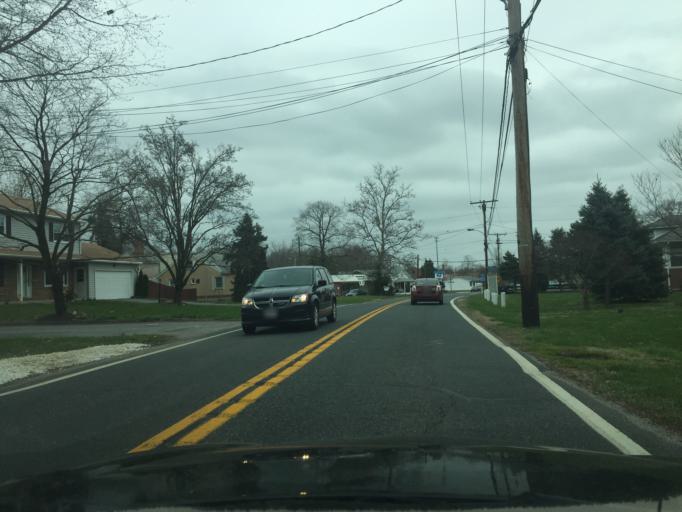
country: US
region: Maryland
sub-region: Baltimore County
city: Bowleys Quarters
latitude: 39.3572
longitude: -76.3729
